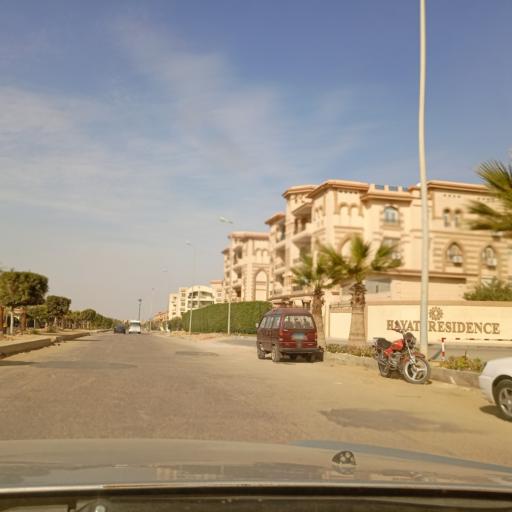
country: EG
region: Muhafazat al Qalyubiyah
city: Al Khankah
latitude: 30.0481
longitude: 31.4852
